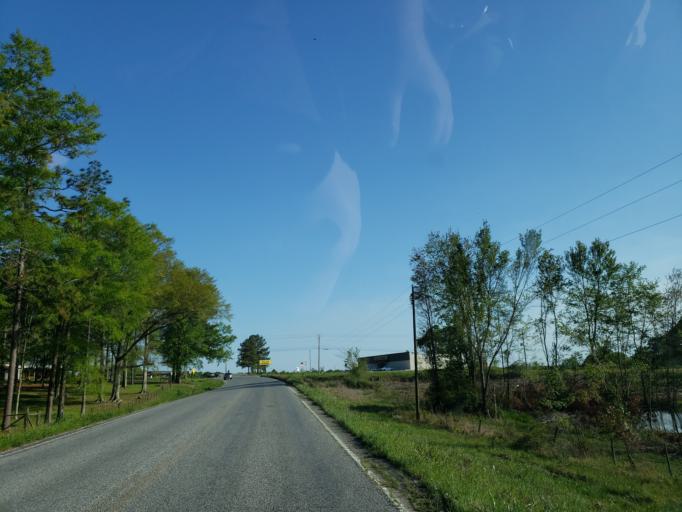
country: US
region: Mississippi
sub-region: Perry County
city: Richton
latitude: 31.4838
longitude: -89.0172
